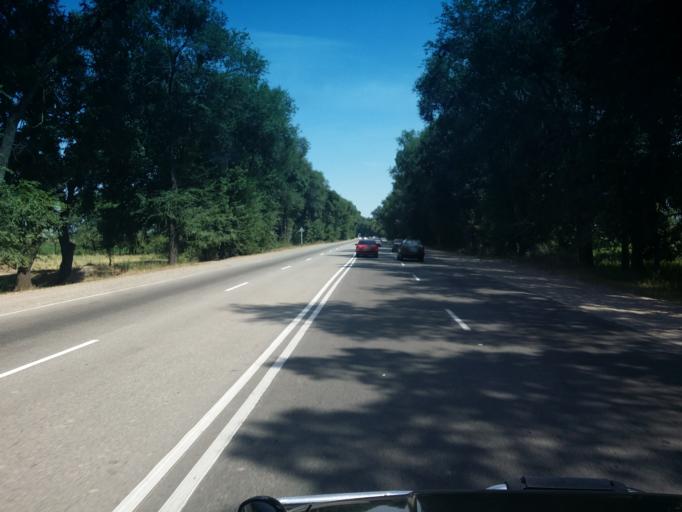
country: KZ
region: Almaty Oblysy
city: Talghar
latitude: 43.4041
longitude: 77.2831
